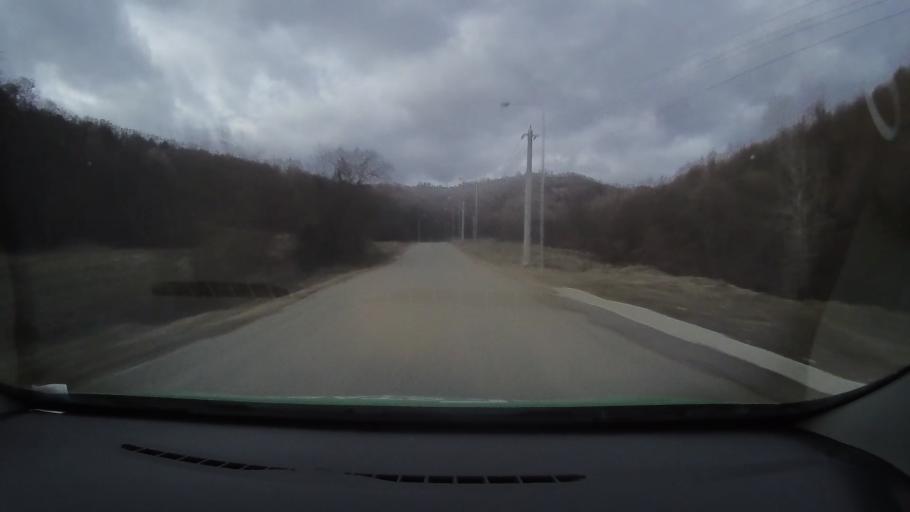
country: RO
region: Prahova
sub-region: Comuna Adunati
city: Adunati
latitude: 45.1276
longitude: 25.6117
